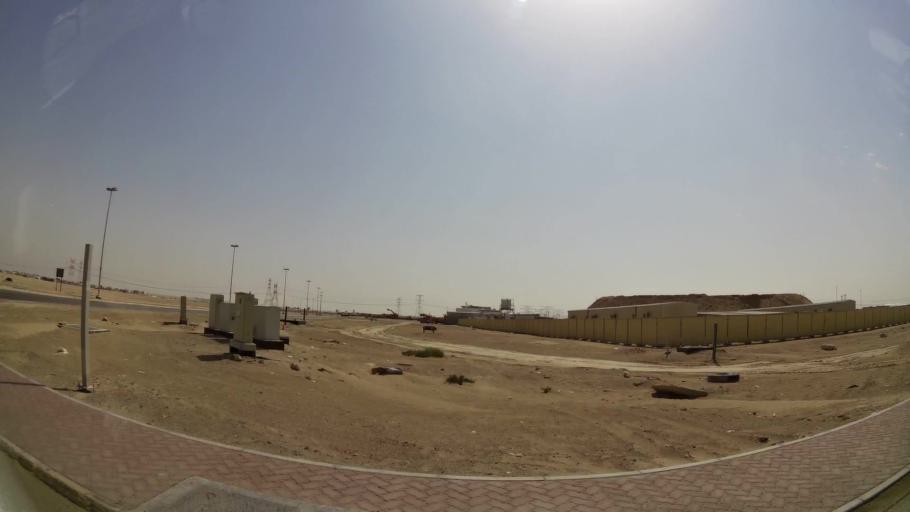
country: AE
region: Abu Dhabi
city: Abu Dhabi
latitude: 24.3046
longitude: 54.5422
